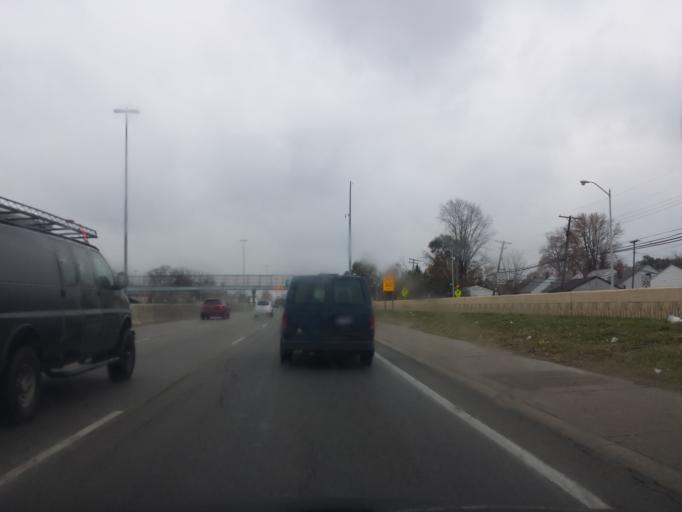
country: US
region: Michigan
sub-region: Wayne County
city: Dearborn
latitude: 42.3477
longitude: -83.2164
